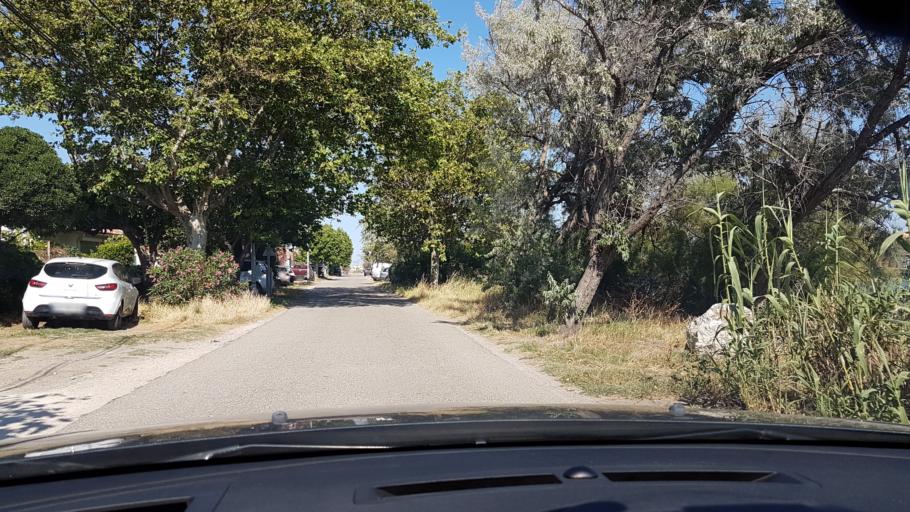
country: FR
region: Provence-Alpes-Cote d'Azur
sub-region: Departement des Bouches-du-Rhone
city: Port-Saint-Louis-du-Rhone
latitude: 43.3888
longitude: 4.8462
